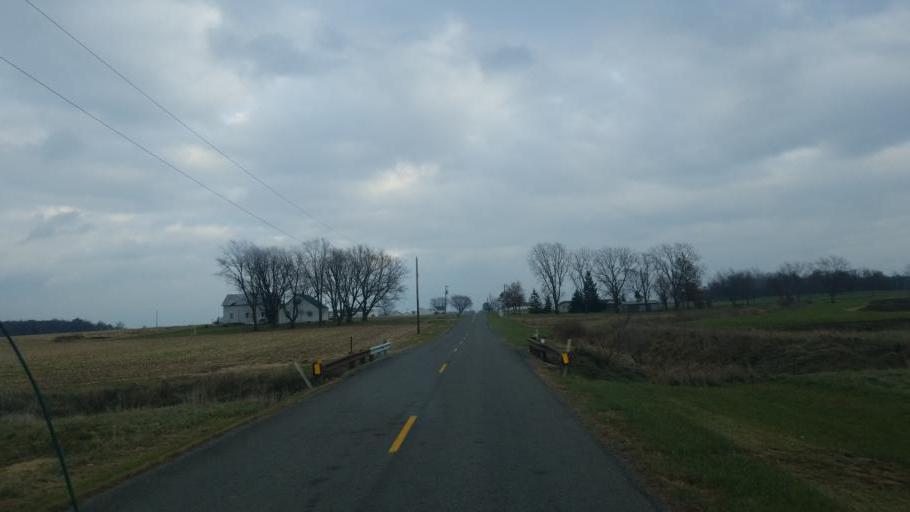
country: US
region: Ohio
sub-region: Mercer County
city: Coldwater
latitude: 40.5090
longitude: -84.6926
